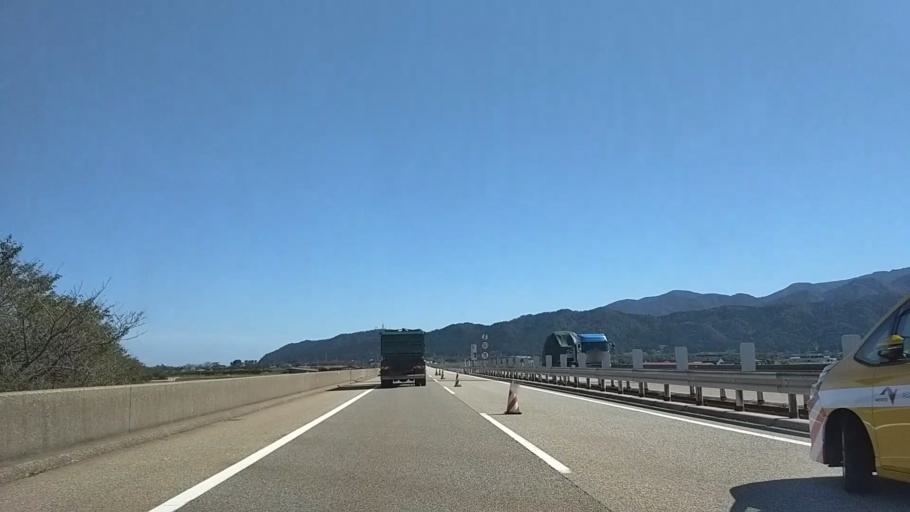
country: JP
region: Toyama
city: Nyuzen
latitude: 36.9342
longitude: 137.5389
